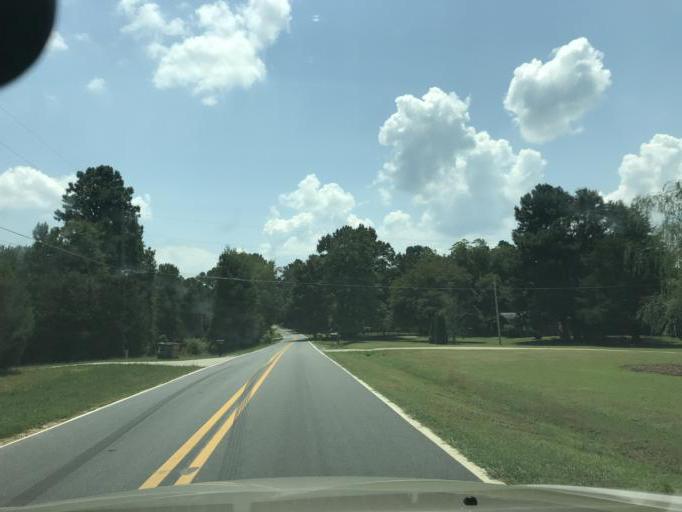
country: US
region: Georgia
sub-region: Forsyth County
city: Cumming
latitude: 34.3035
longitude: -84.1828
